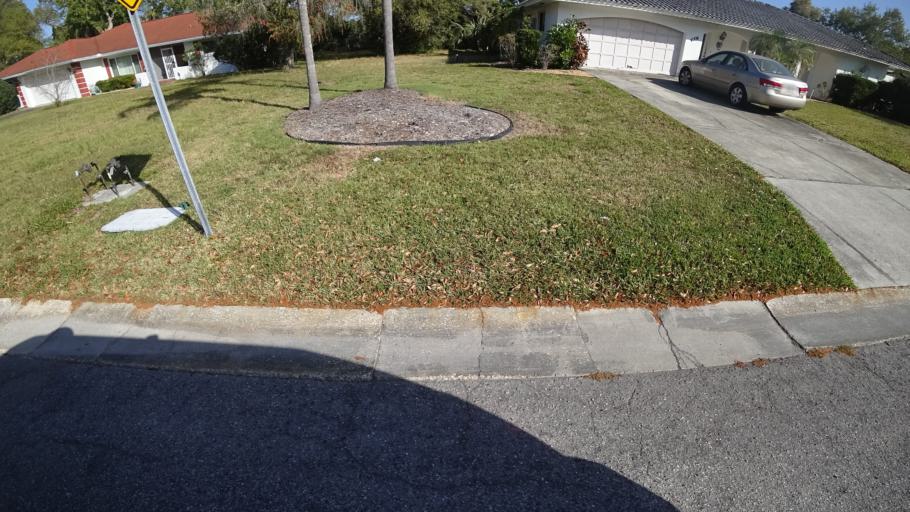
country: US
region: Florida
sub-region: Manatee County
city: Whitfield
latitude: 27.4131
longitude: -82.5642
